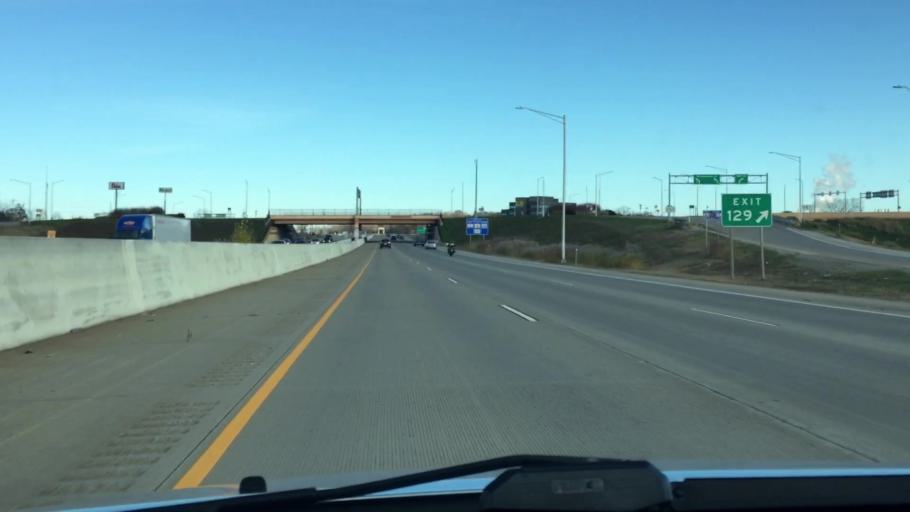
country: US
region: Wisconsin
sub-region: Winnebago County
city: Neenah
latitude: 44.1539
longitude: -88.4862
